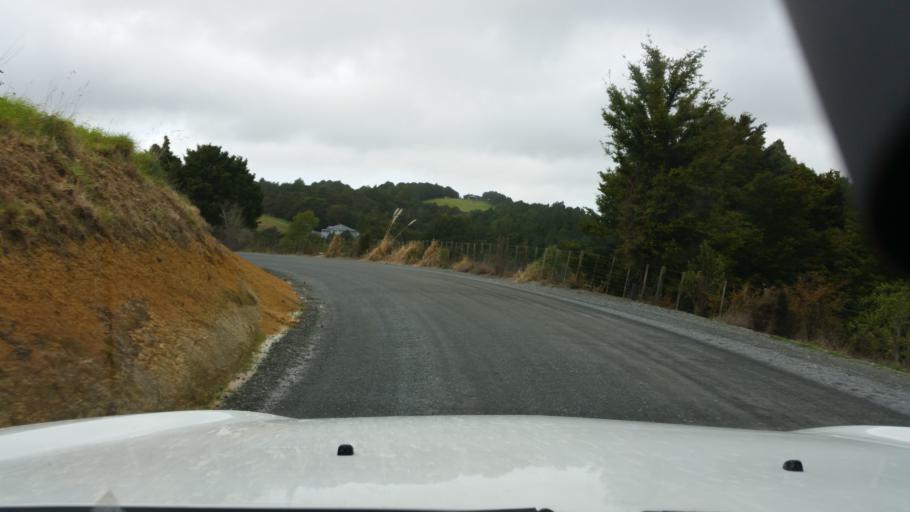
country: NZ
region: Northland
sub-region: Whangarei
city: Whangarei
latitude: -35.7326
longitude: 174.4220
